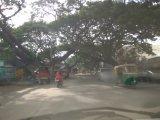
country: IN
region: Karnataka
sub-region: Bangalore Urban
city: Bangalore
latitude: 12.9861
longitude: 77.5414
